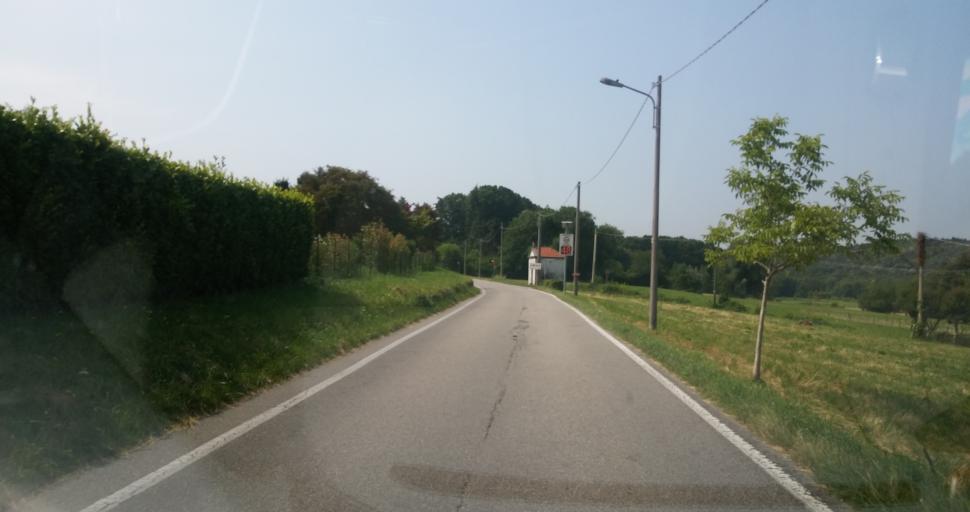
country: IT
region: Lombardy
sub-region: Provincia di Varese
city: Osmate
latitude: 45.7721
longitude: 8.6536
